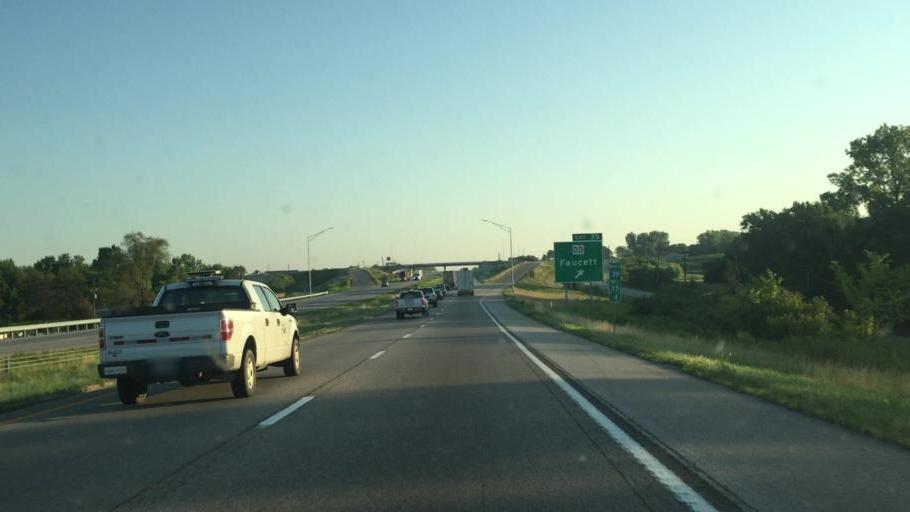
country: US
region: Kansas
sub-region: Doniphan County
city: Elwood
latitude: 39.5951
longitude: -94.7887
